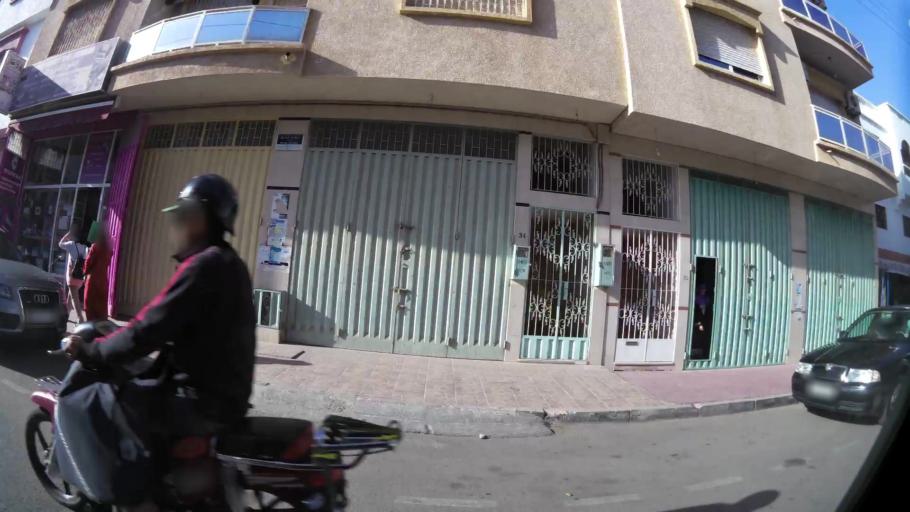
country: MA
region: Oued ed Dahab-Lagouira
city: Dakhla
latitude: 30.4018
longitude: -9.5522
